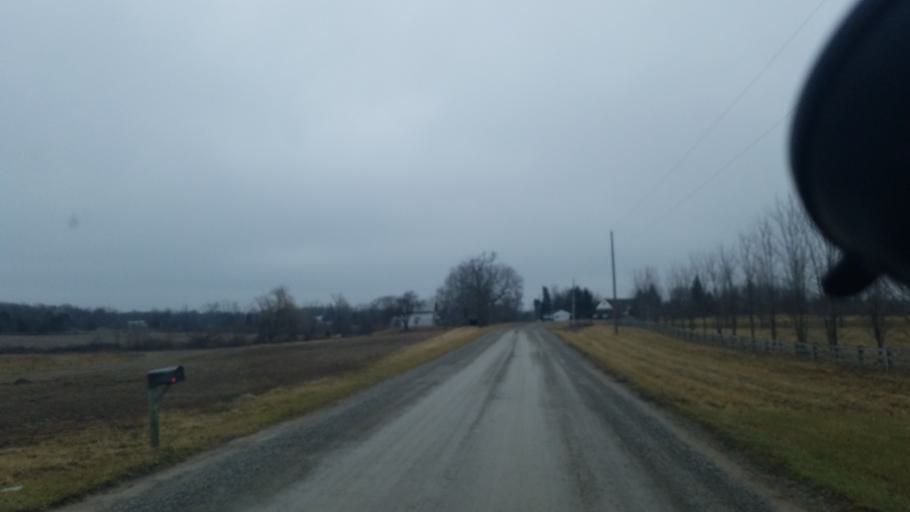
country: US
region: Ohio
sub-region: Morrow County
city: Mount Gilead
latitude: 40.5089
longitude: -82.7061
